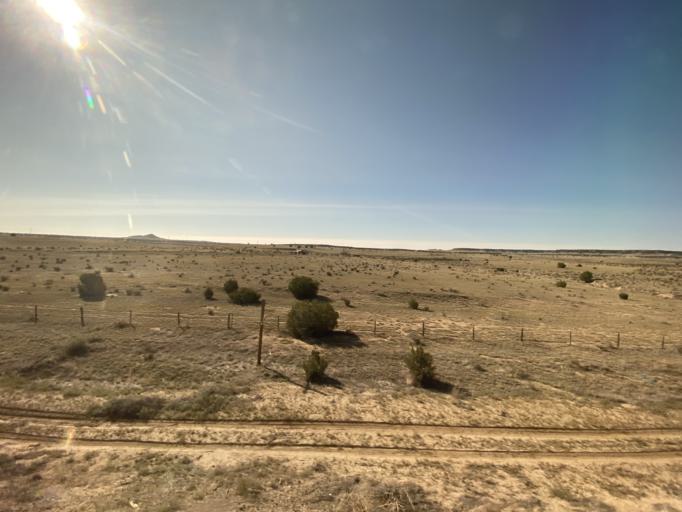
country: US
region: Colorado
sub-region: Otero County
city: Fowler
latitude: 37.5719
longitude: -104.0563
